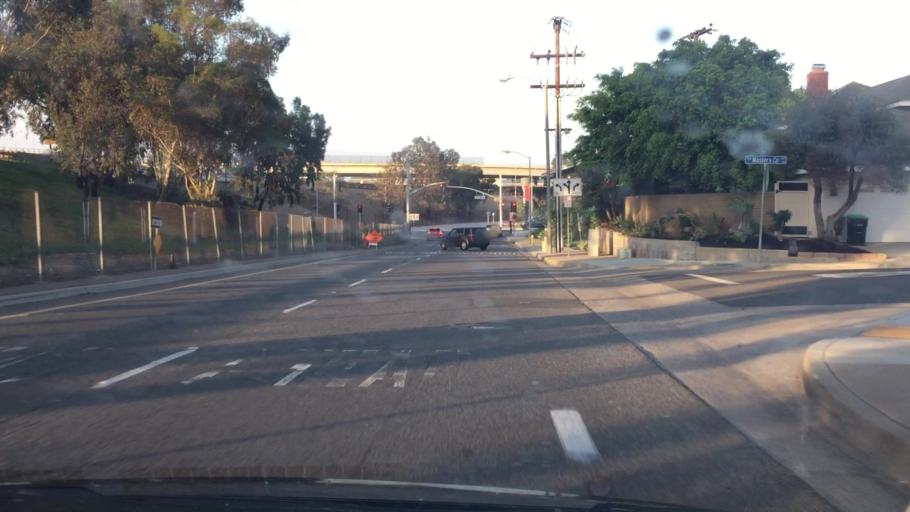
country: US
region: California
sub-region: Orange County
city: Costa Mesa
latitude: 33.6706
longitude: -117.8885
